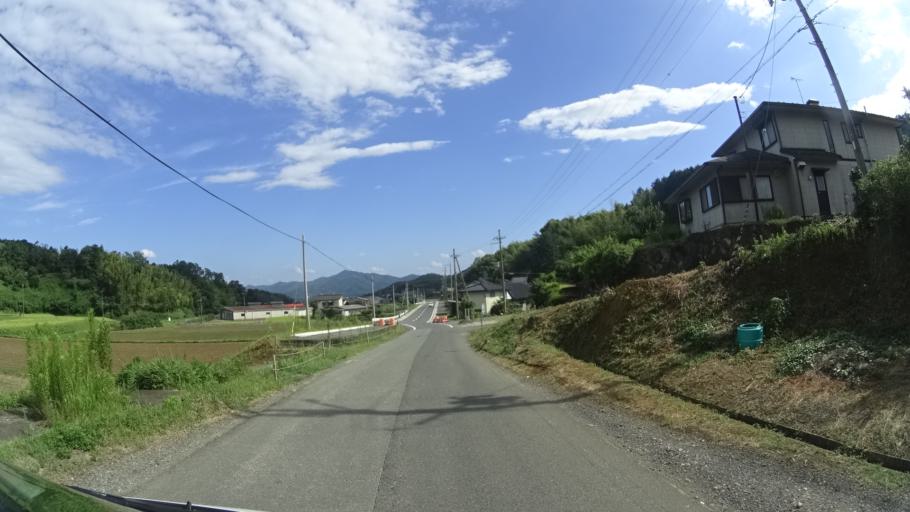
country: JP
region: Kyoto
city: Fukuchiyama
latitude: 35.3349
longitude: 135.1708
